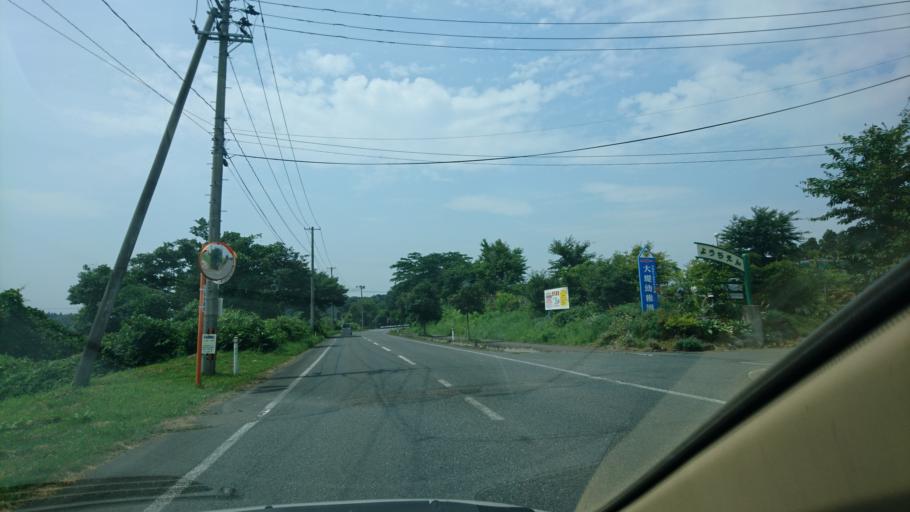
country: JP
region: Iwate
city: Kitakami
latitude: 39.2568
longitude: 141.0847
